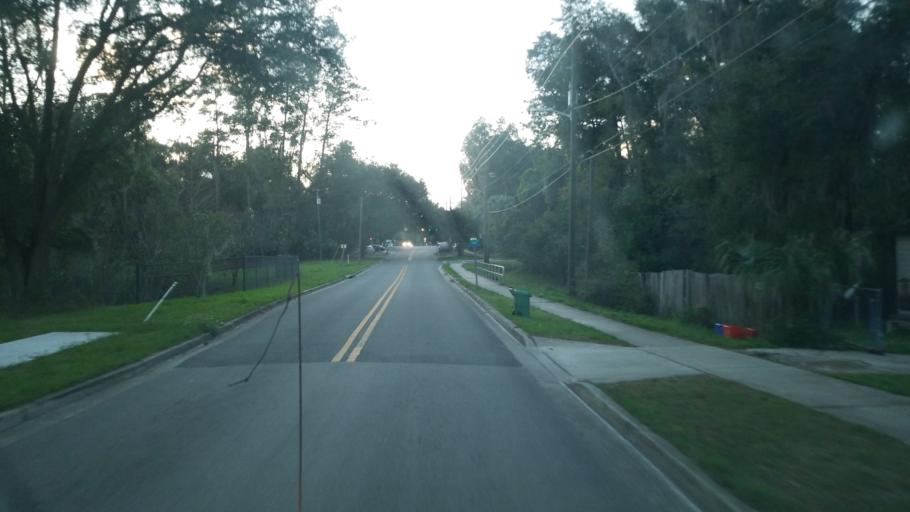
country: US
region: Florida
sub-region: Alachua County
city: Gainesville
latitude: 29.6501
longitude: -82.3090
